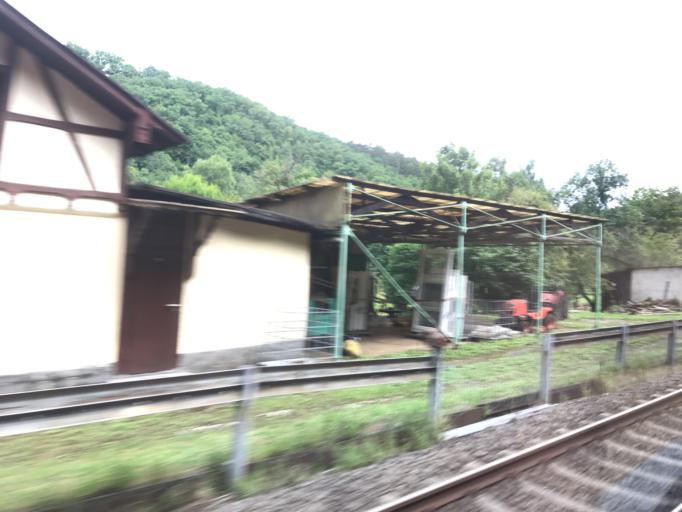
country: DE
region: Rheinland-Pfalz
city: Gutenacker
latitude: 50.3286
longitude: 7.9302
